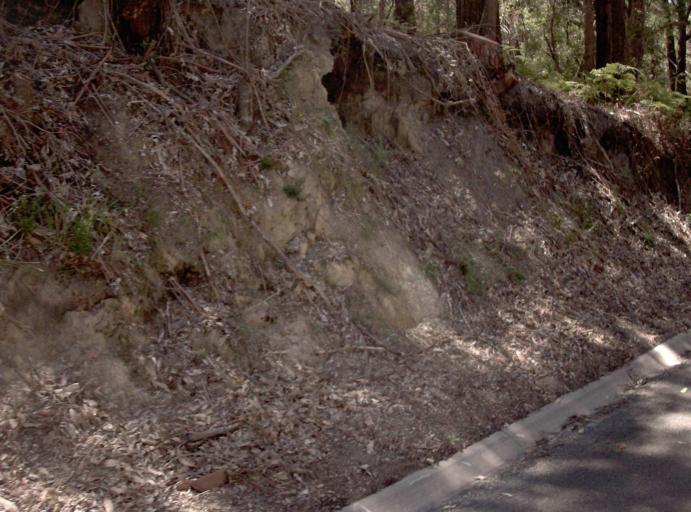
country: AU
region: Victoria
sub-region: East Gippsland
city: Lakes Entrance
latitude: -37.7068
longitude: 148.7025
